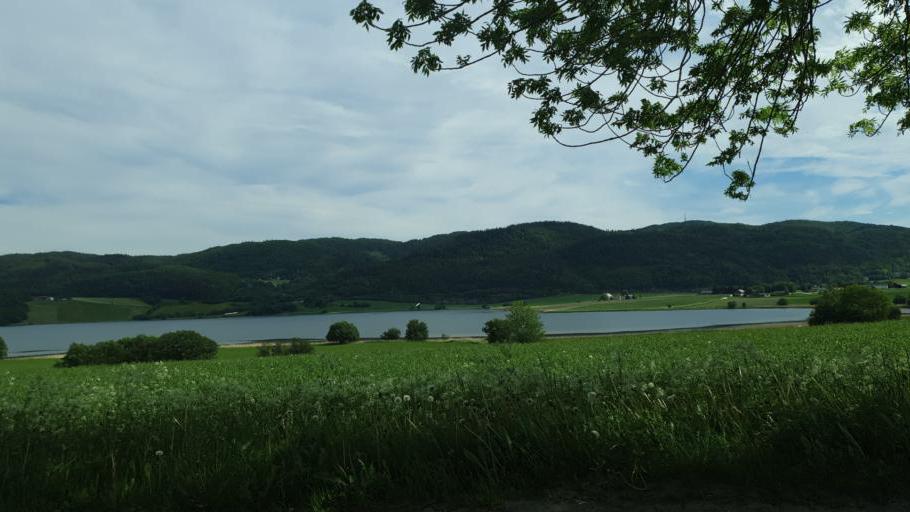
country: NO
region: Sor-Trondelag
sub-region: Rissa
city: Rissa
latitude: 63.5673
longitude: 9.9303
